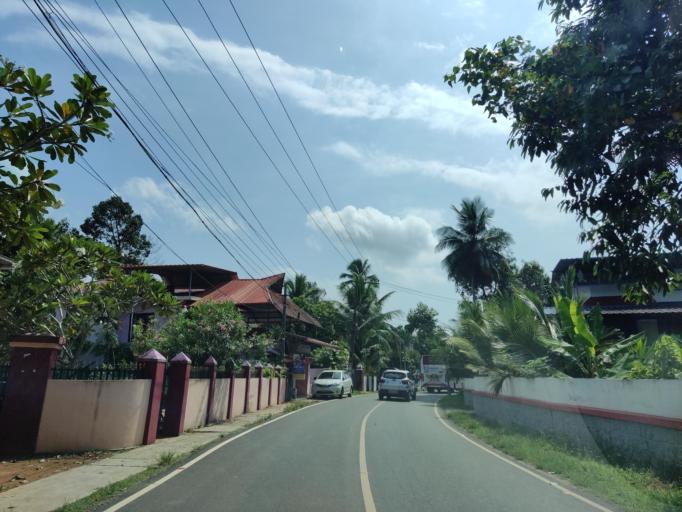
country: IN
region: Kerala
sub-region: Alappuzha
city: Mavelikara
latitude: 9.3227
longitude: 76.5168
